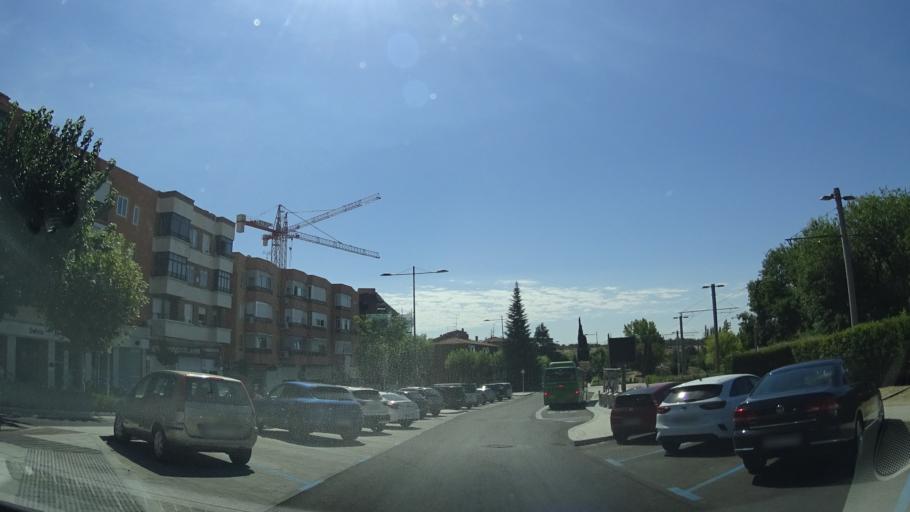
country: ES
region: Madrid
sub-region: Provincia de Madrid
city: Boadilla del Monte
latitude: 40.4054
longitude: -3.8780
